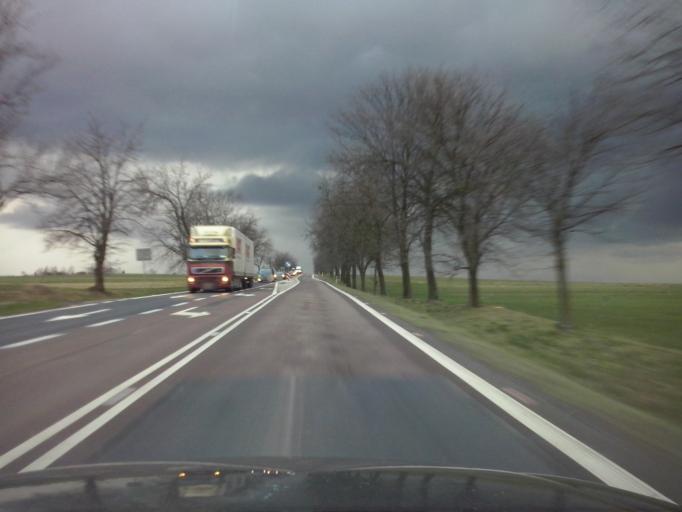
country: PL
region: Lublin Voivodeship
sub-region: Powiat chelmski
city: Rejowiec Fabryczny
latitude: 51.1777
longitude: 23.2203
